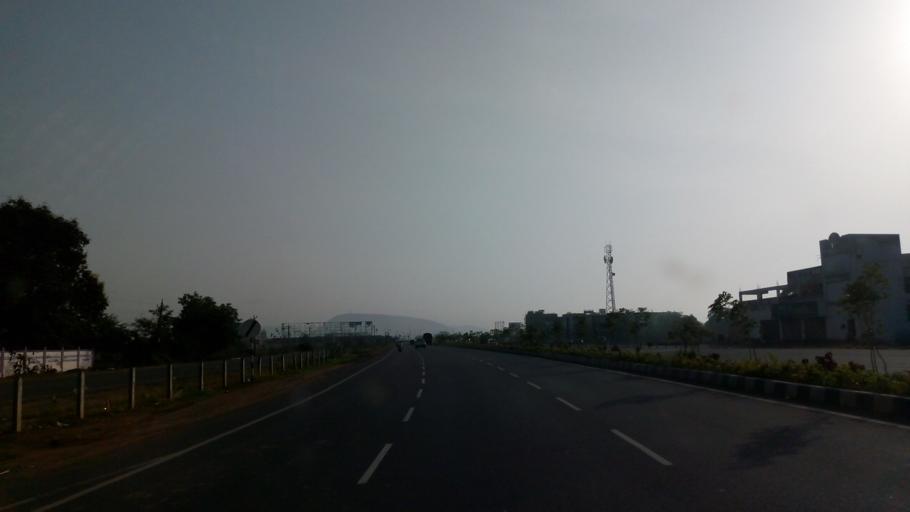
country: IN
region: Andhra Pradesh
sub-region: Guntur
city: Mangalagiri
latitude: 16.3987
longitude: 80.5494
